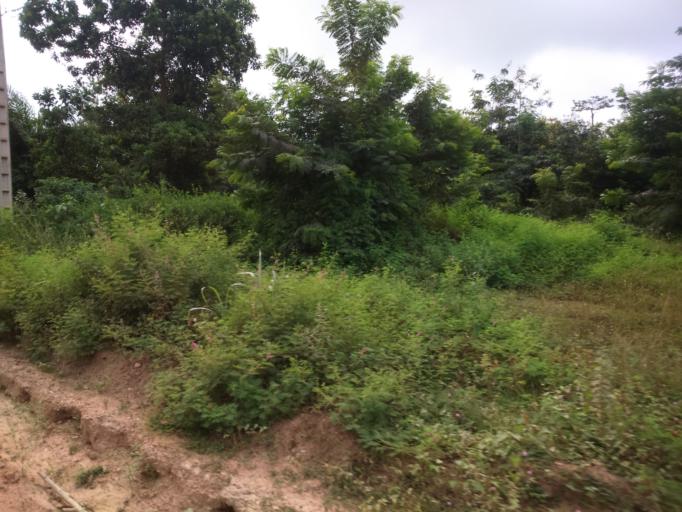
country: CI
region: Agneby
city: Agboville
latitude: 6.0106
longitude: -4.1482
